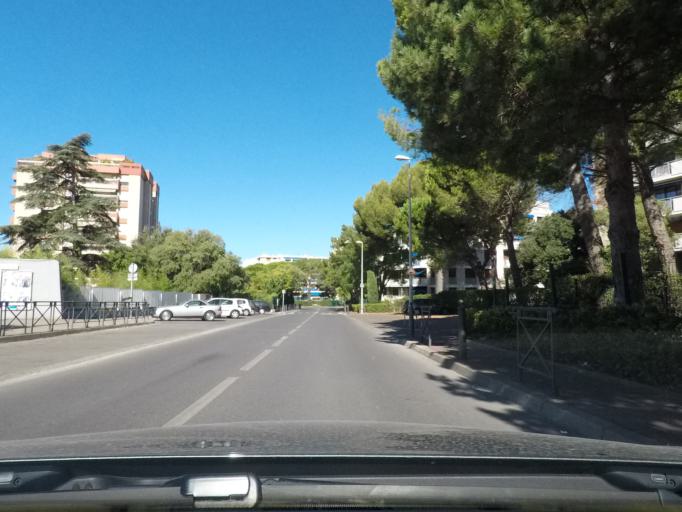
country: FR
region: Provence-Alpes-Cote d'Azur
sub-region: Departement des Bouches-du-Rhone
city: Marseille 09
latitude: 43.2538
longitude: 5.4155
